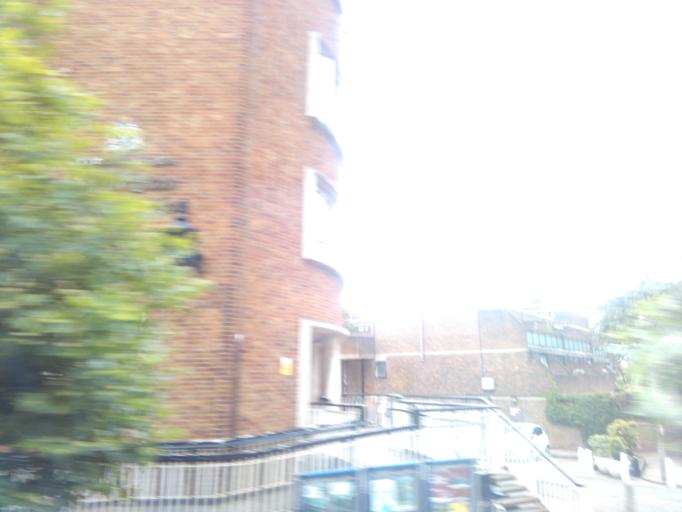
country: GB
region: England
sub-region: Greater London
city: Lambeth
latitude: 51.4973
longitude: -0.1116
